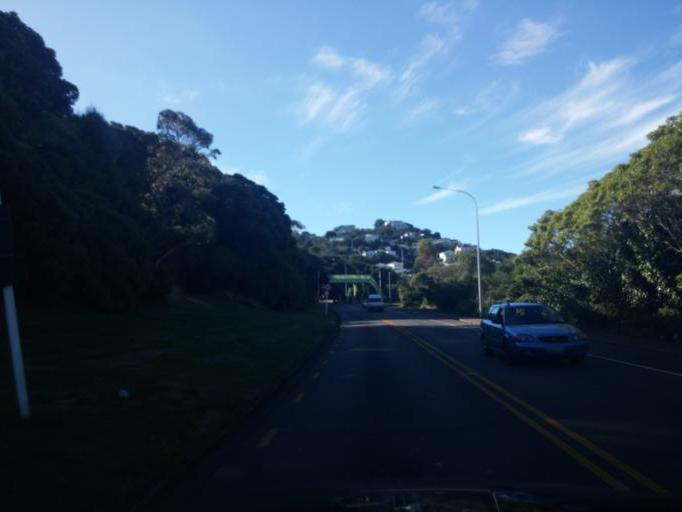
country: NZ
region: Wellington
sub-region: Wellington City
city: Wellington
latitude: -41.3063
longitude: 174.7924
